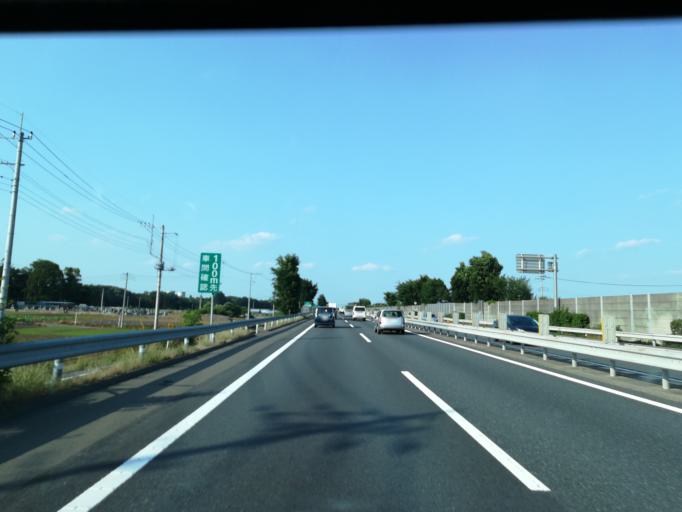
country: JP
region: Saitama
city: Sayama
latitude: 35.8541
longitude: 139.3683
